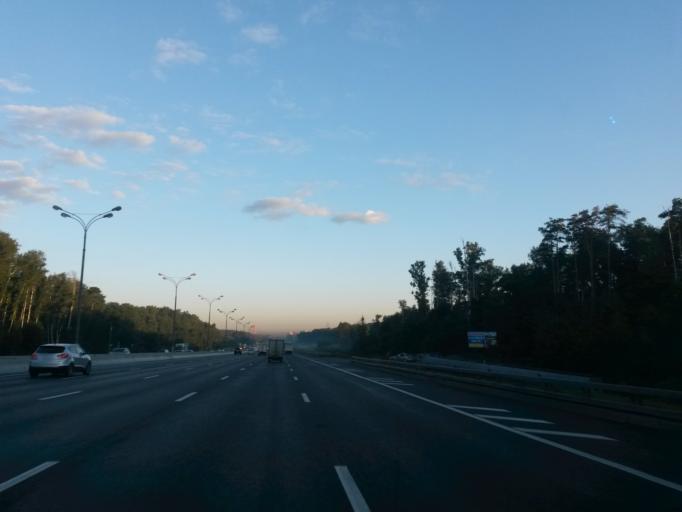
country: RU
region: Moskovskaya
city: Druzhba
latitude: 55.8615
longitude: 37.7671
